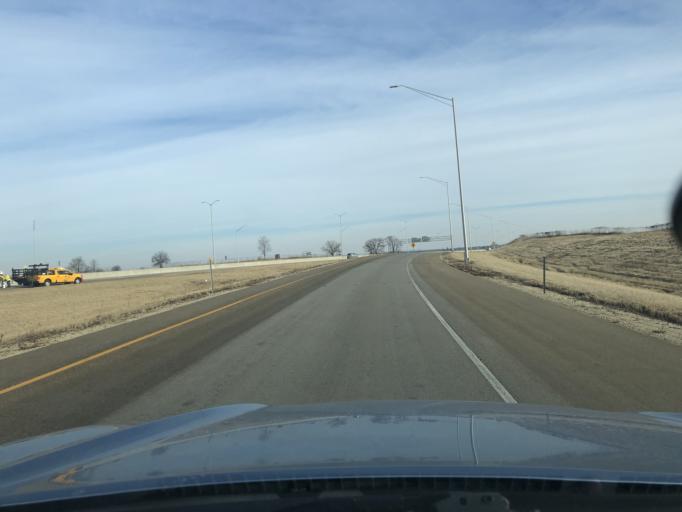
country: US
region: Illinois
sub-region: Boone County
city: Belvidere
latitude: 42.2331
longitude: -88.8119
